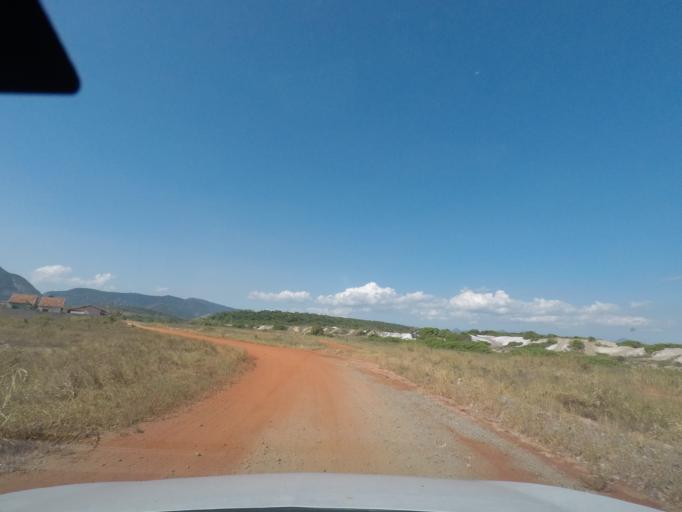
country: BR
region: Rio de Janeiro
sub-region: Marica
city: Marica
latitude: -22.9683
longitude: -42.9040
